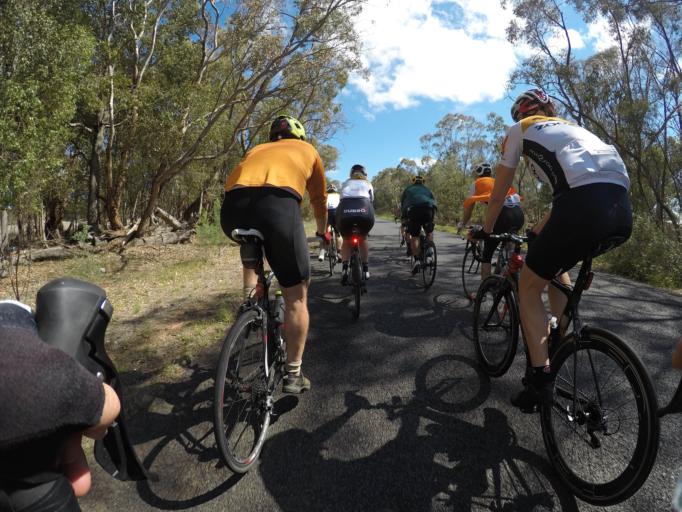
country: AU
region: New South Wales
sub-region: Dubbo Municipality
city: Eulomogo
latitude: -32.6056
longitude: 148.5468
